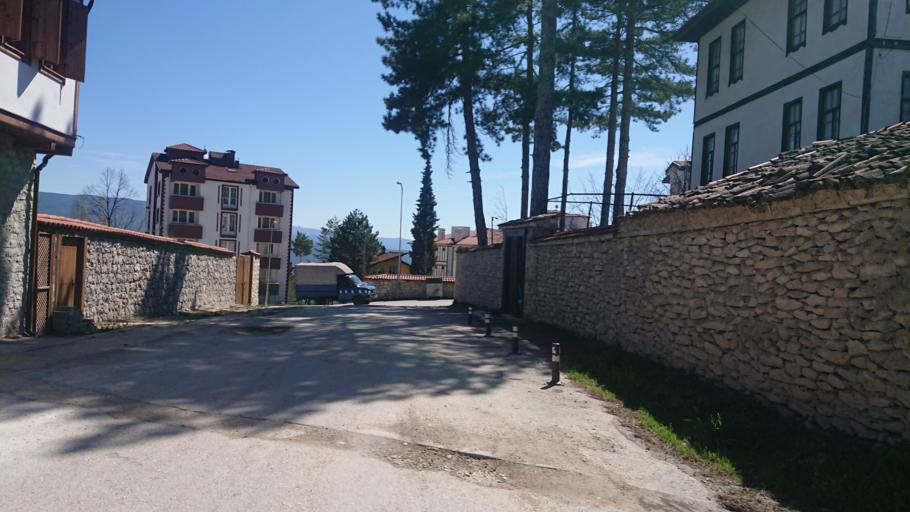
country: TR
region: Karabuk
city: Safranbolu
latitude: 41.2589
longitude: 32.6754
